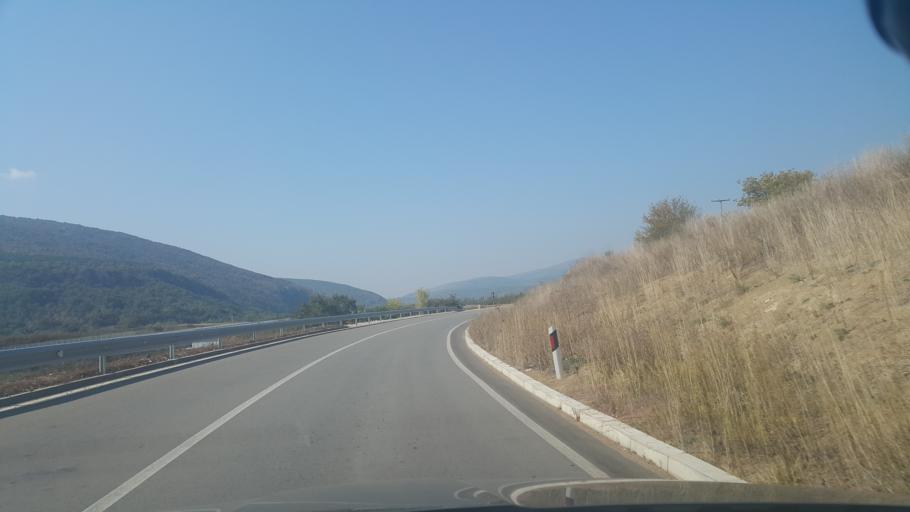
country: RS
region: Central Serbia
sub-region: Pirotski Okrug
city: Pirot
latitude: 43.2146
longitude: 22.5087
